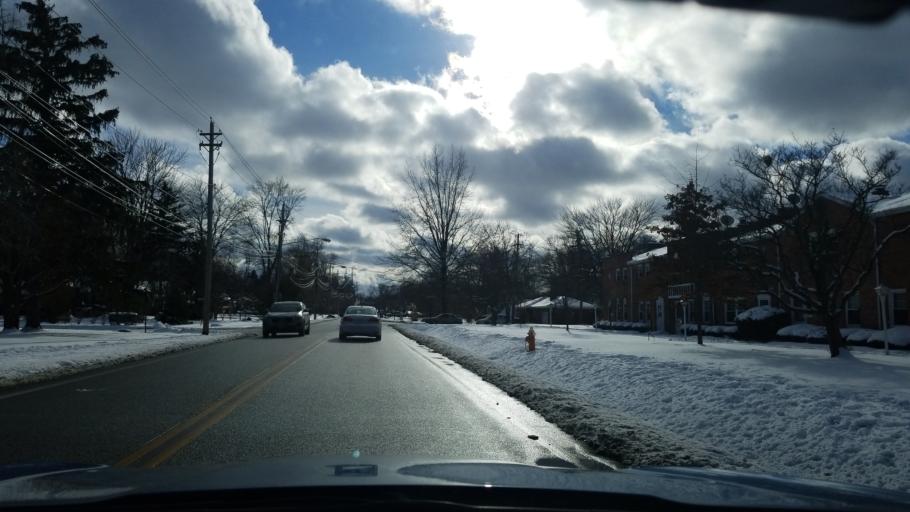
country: US
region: Ohio
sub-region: Cuyahoga County
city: North Olmsted
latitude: 41.4183
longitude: -81.8927
